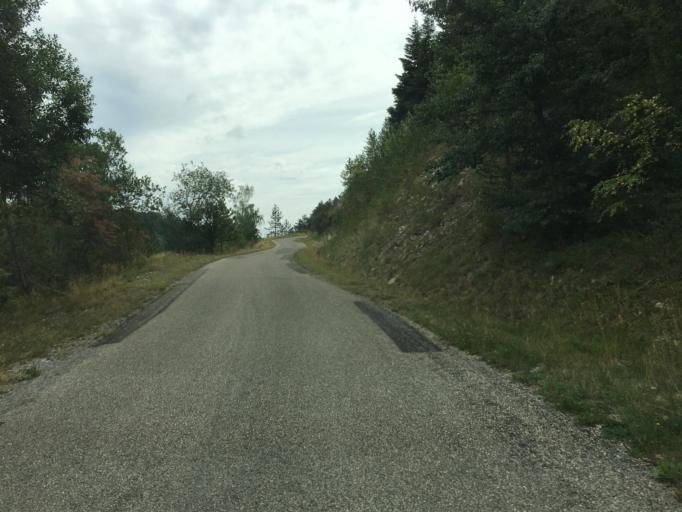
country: FR
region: Provence-Alpes-Cote d'Azur
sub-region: Departement des Alpes-de-Haute-Provence
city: Digne-les-Bains
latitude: 44.2205
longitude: 6.1392
